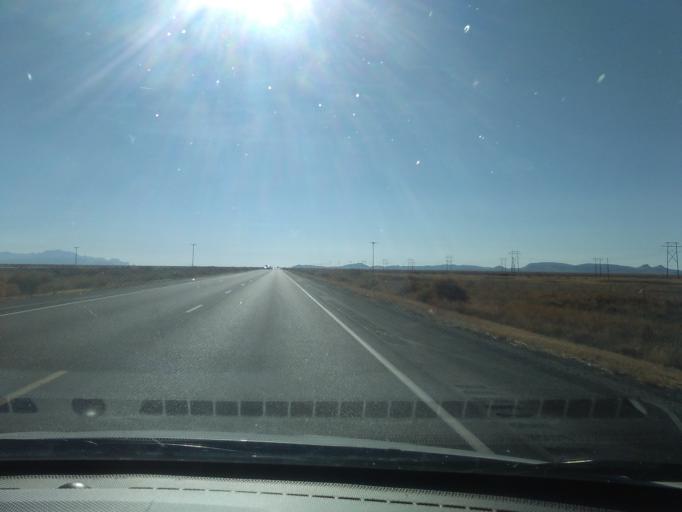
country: US
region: New Mexico
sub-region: Luna County
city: Deming
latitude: 32.5194
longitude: -107.4981
